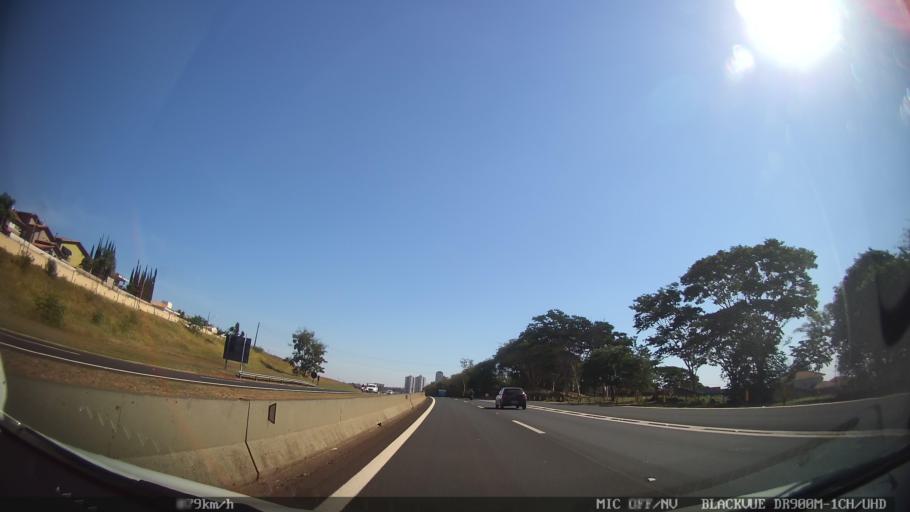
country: BR
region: Sao Paulo
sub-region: Ribeirao Preto
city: Ribeirao Preto
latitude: -21.2213
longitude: -47.7842
